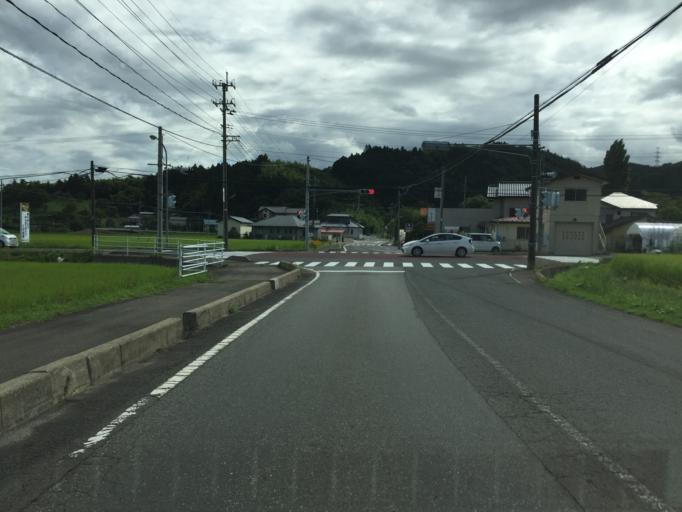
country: JP
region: Fukushima
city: Nihommatsu
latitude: 37.6659
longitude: 140.4227
